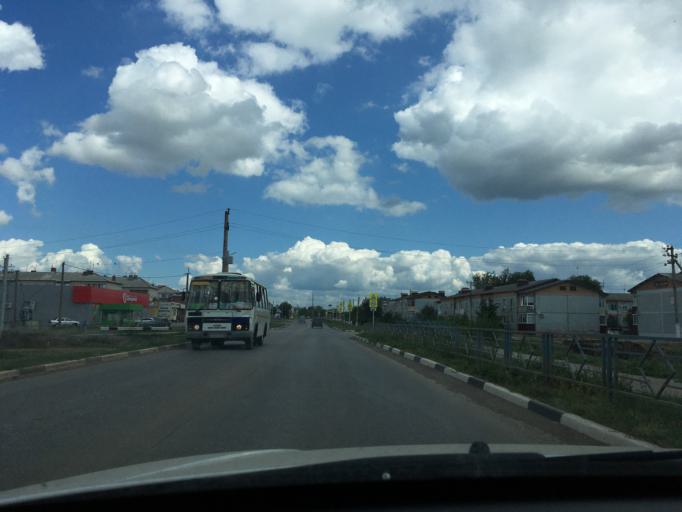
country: RU
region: Samara
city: Bezenchuk
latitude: 52.9926
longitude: 49.4372
